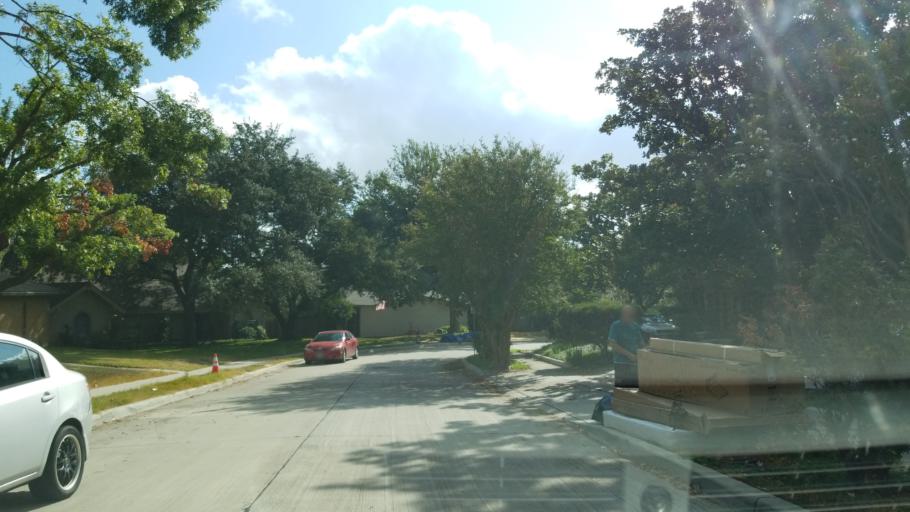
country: US
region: Texas
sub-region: Dallas County
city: Richardson
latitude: 32.9310
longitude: -96.7673
